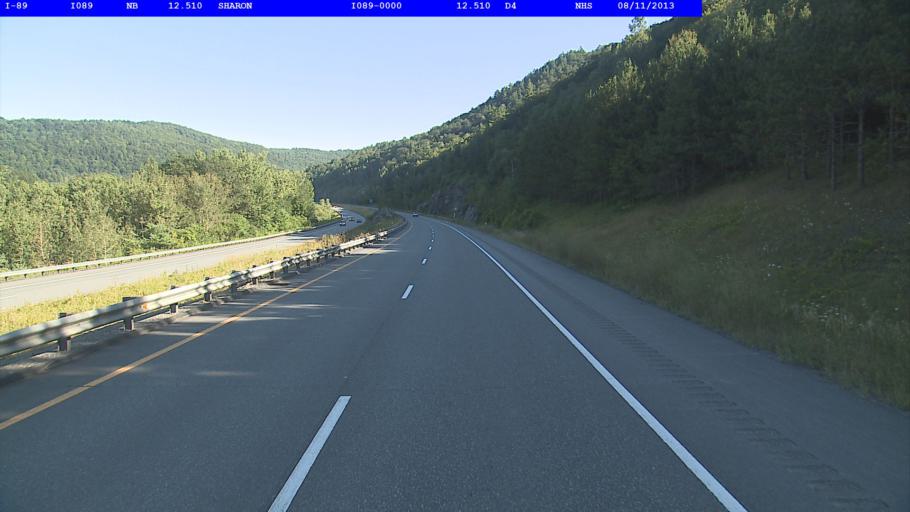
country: US
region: Vermont
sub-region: Windsor County
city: Woodstock
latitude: 43.7753
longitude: -72.4445
